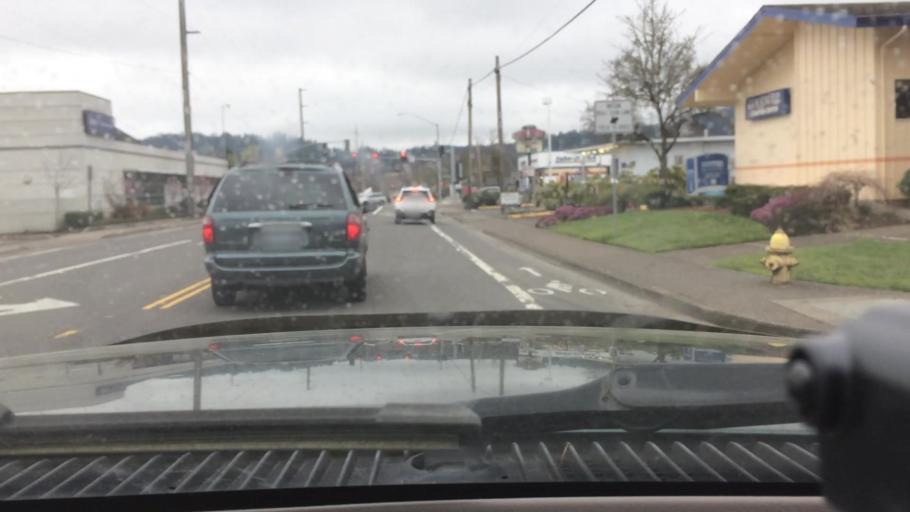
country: US
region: Oregon
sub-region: Lane County
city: Eugene
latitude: 44.0262
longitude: -123.0921
